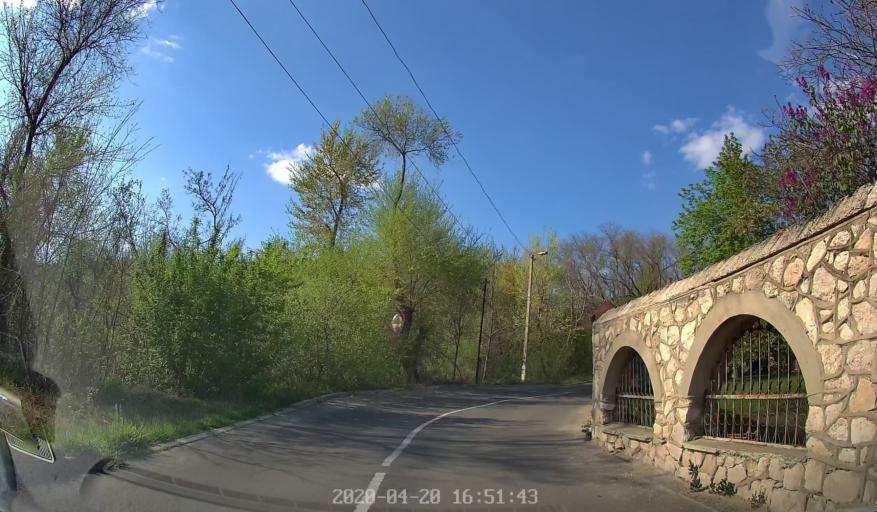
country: MD
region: Chisinau
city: Chisinau
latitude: 46.9683
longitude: 28.8507
